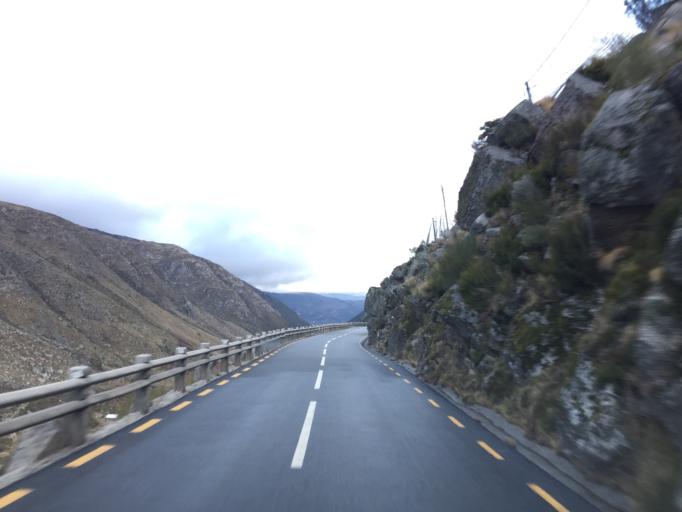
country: PT
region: Guarda
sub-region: Manteigas
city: Manteigas
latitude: 40.3365
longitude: -7.5685
